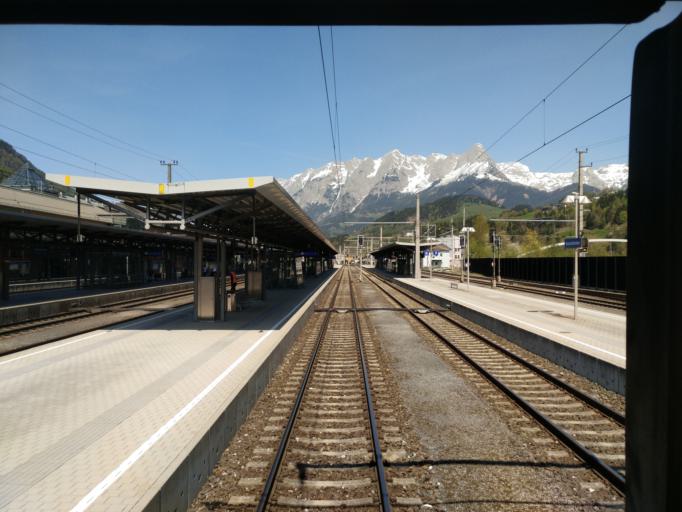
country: AT
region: Salzburg
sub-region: Politischer Bezirk Sankt Johann im Pongau
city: Bischofshofen
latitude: 47.4171
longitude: 13.2203
